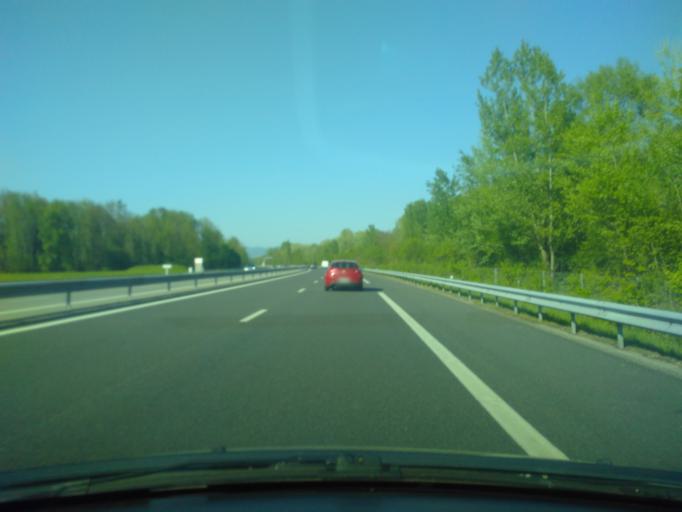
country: FR
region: Rhone-Alpes
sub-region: Departement de l'Isere
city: Saint-Quentin-sur-Isere
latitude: 45.2428
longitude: 5.4997
